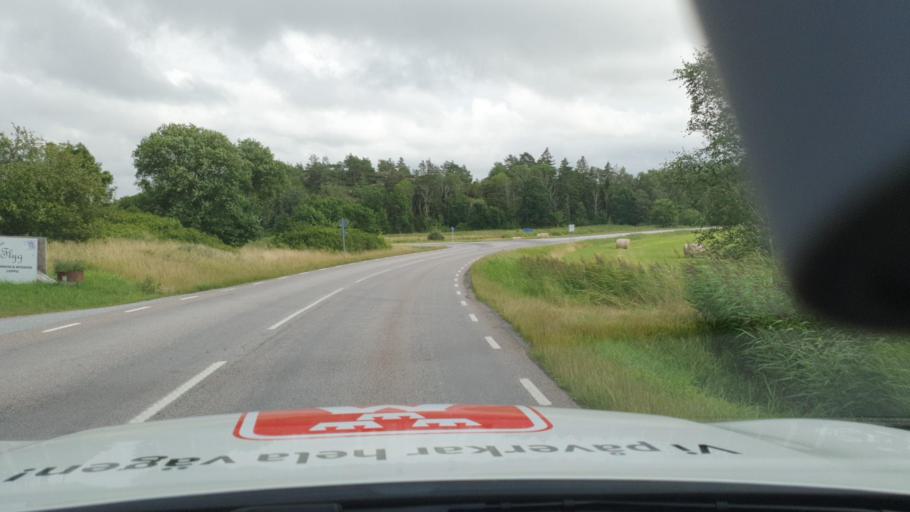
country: SE
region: Vaestra Goetaland
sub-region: Tanums Kommun
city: Grebbestad
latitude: 58.5944
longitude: 11.3138
